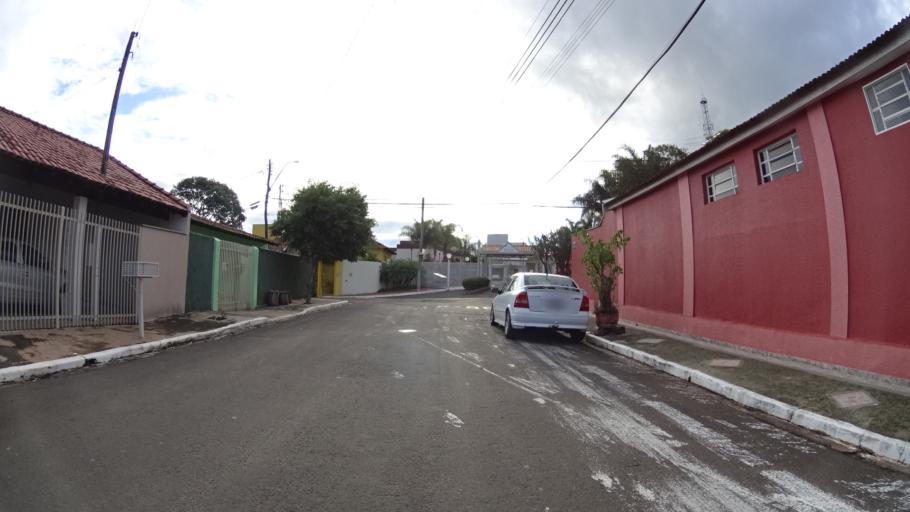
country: BR
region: Sao Paulo
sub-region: Marilia
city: Marilia
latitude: -22.2227
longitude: -49.8897
